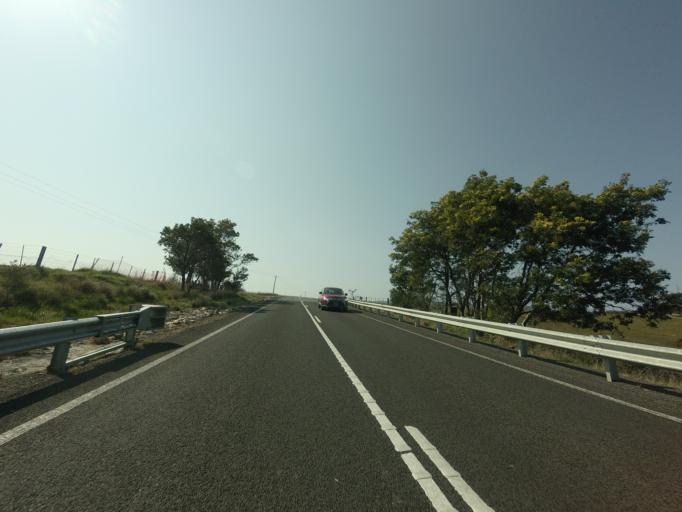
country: AU
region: Tasmania
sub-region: Northern Midlands
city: Evandale
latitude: -41.8041
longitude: 147.6836
